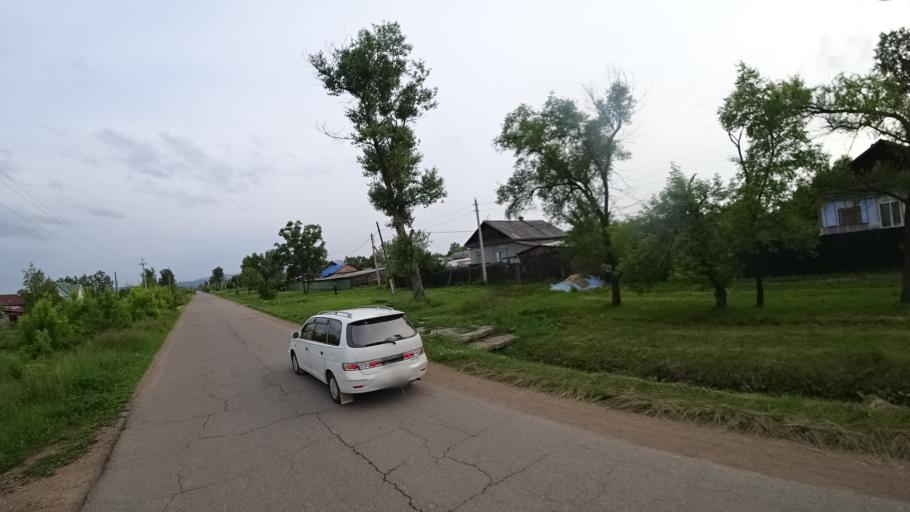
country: RU
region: Primorskiy
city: Novosysoyevka
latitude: 44.2422
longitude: 133.3678
